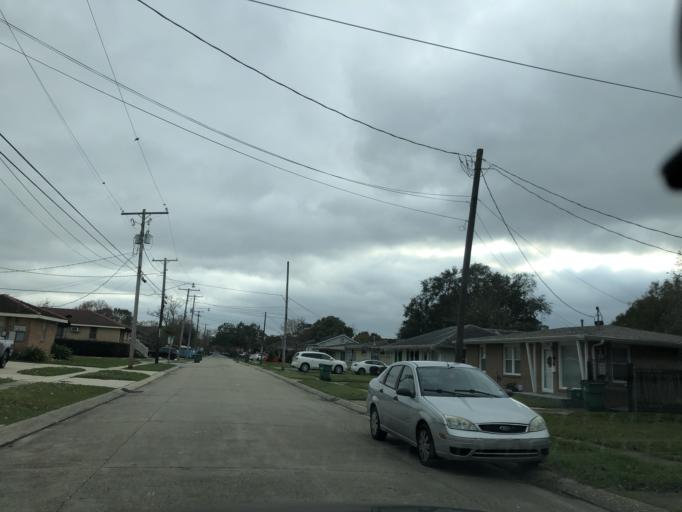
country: US
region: Louisiana
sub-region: Jefferson Parish
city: Metairie
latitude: 29.9915
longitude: -90.1577
